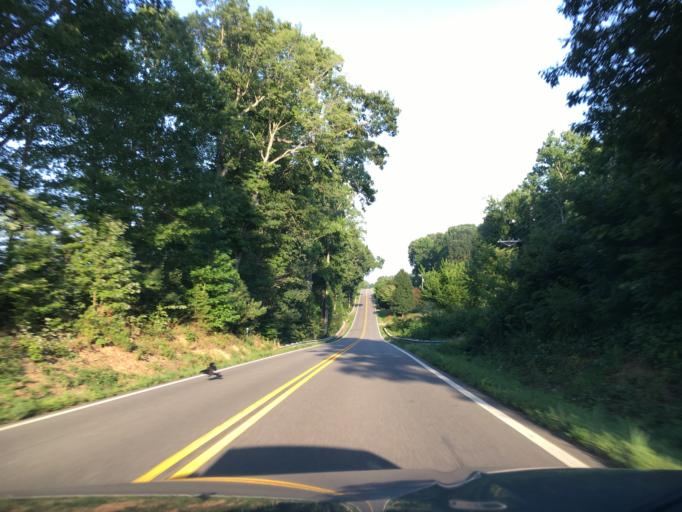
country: US
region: Virginia
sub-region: Halifax County
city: Mountain Road
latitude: 36.8336
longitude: -79.1242
